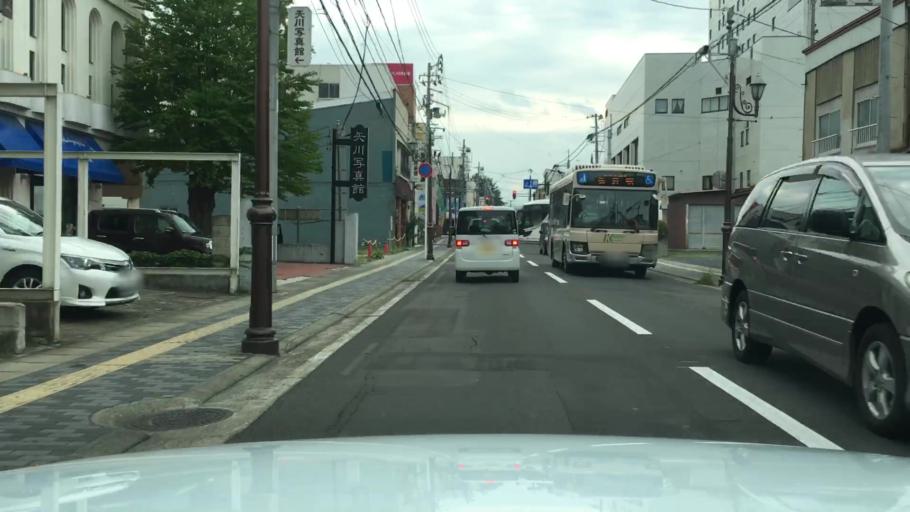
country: JP
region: Aomori
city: Hirosaki
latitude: 40.5991
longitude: 140.4770
